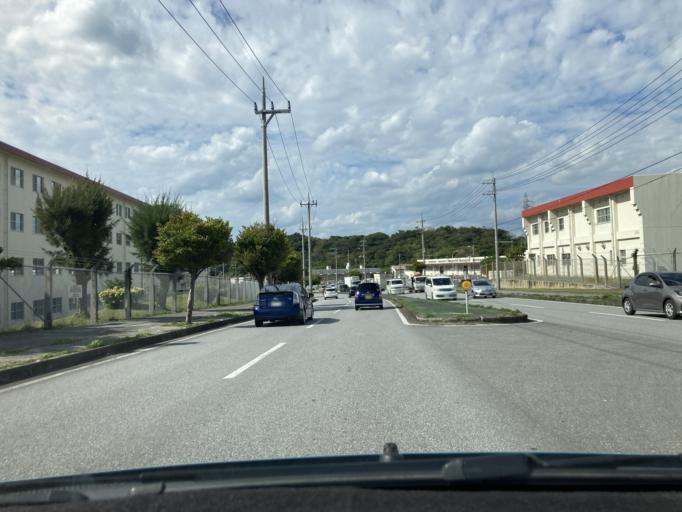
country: JP
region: Okinawa
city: Chatan
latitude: 26.3067
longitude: 127.7707
